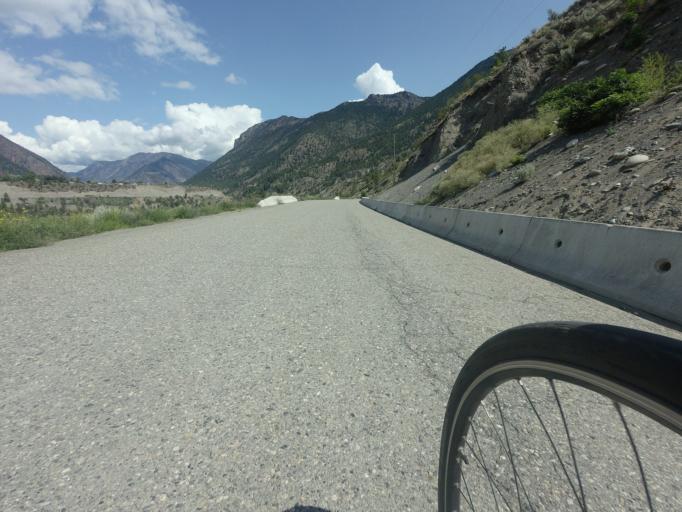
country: CA
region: British Columbia
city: Lillooet
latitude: 50.7045
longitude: -121.9125
